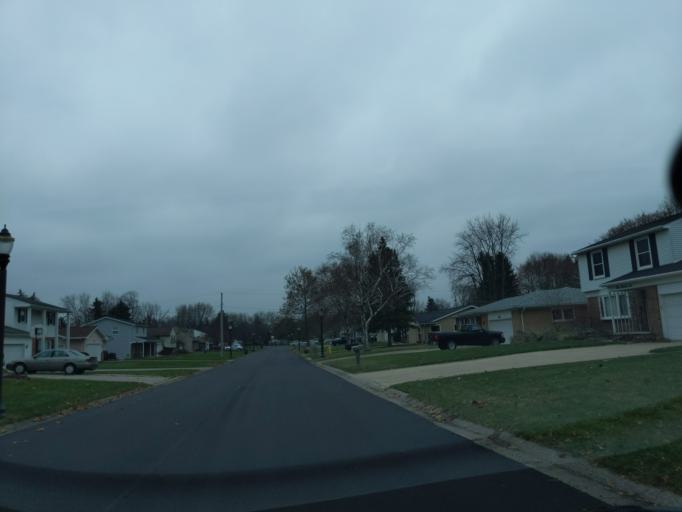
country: US
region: Michigan
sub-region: Eaton County
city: Waverly
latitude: 42.7312
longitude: -84.6293
